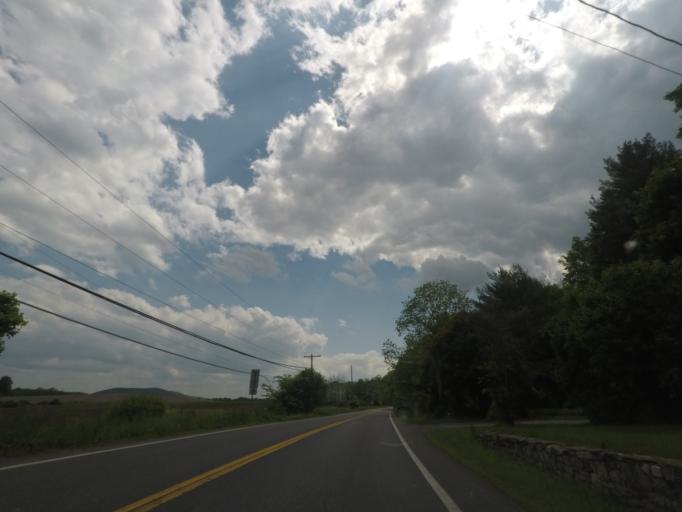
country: US
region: New York
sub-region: Dutchess County
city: Dover Plains
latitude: 41.8810
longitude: -73.5290
